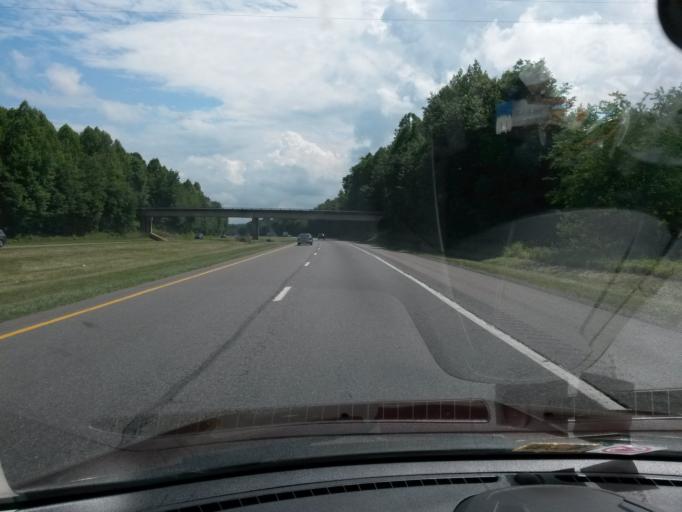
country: US
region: North Carolina
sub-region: Surry County
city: Dobson
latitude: 36.3644
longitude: -80.7978
